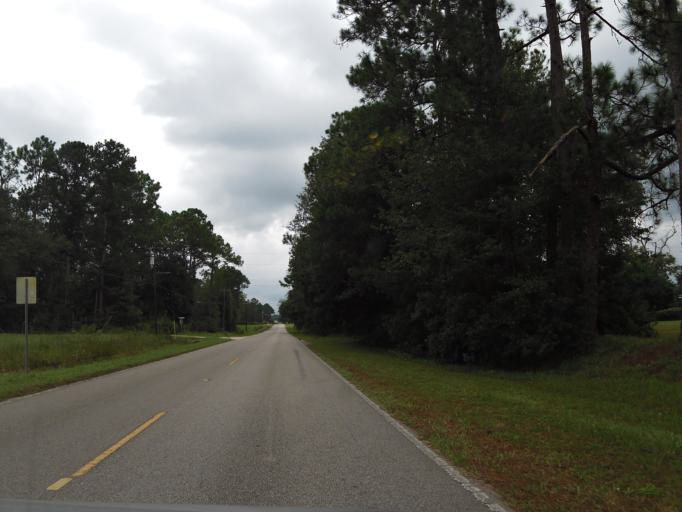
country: US
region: Florida
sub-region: Clay County
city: Middleburg
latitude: 30.1127
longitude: -81.9491
